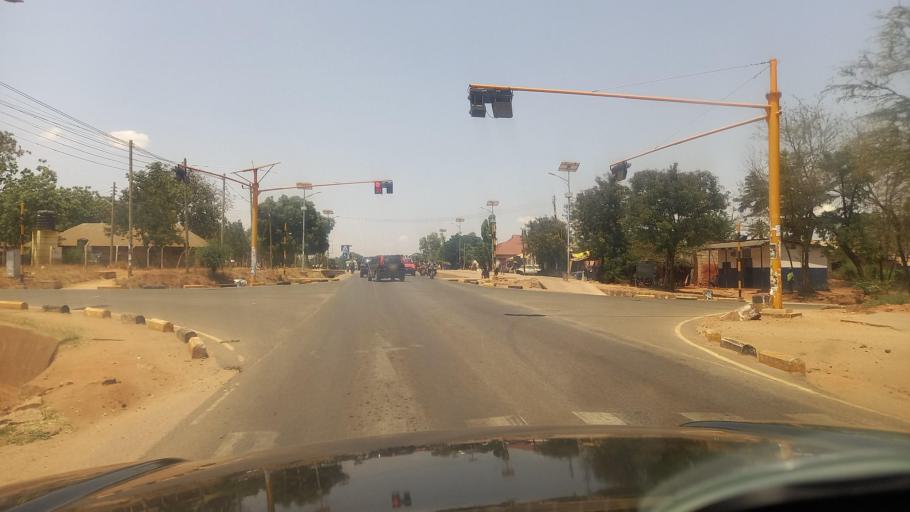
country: TZ
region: Morogoro
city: Morogoro
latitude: -6.8121
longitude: 37.6646
